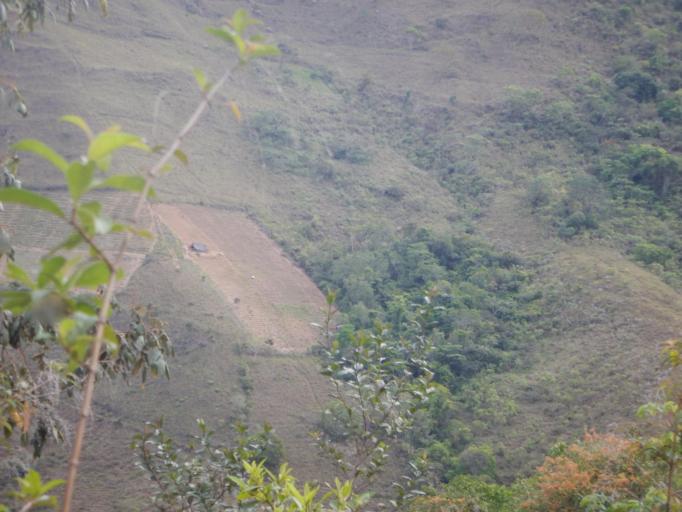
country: BO
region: La Paz
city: Coroico
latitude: -16.1531
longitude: -67.7367
